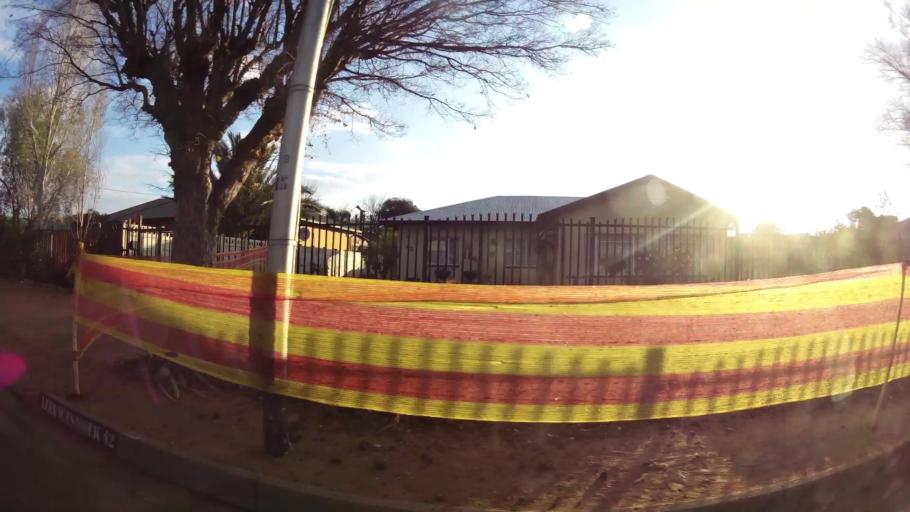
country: ZA
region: Orange Free State
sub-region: Mangaung Metropolitan Municipality
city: Bloemfontein
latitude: -29.1358
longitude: 26.1960
